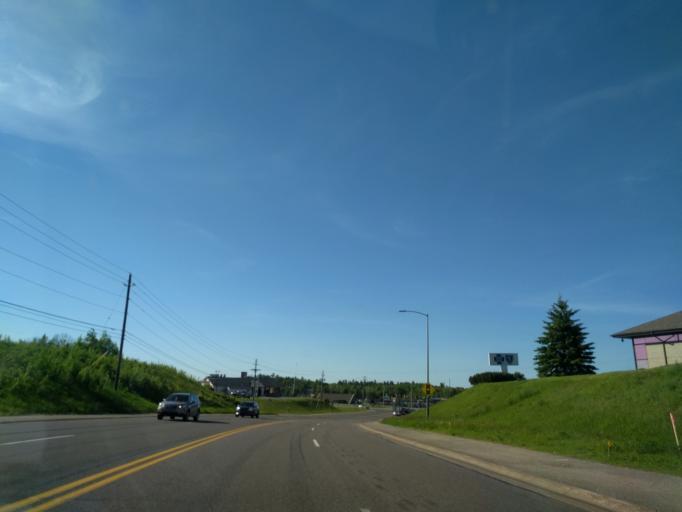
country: US
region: Michigan
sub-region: Marquette County
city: Trowbridge Park
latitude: 46.5413
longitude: -87.4194
